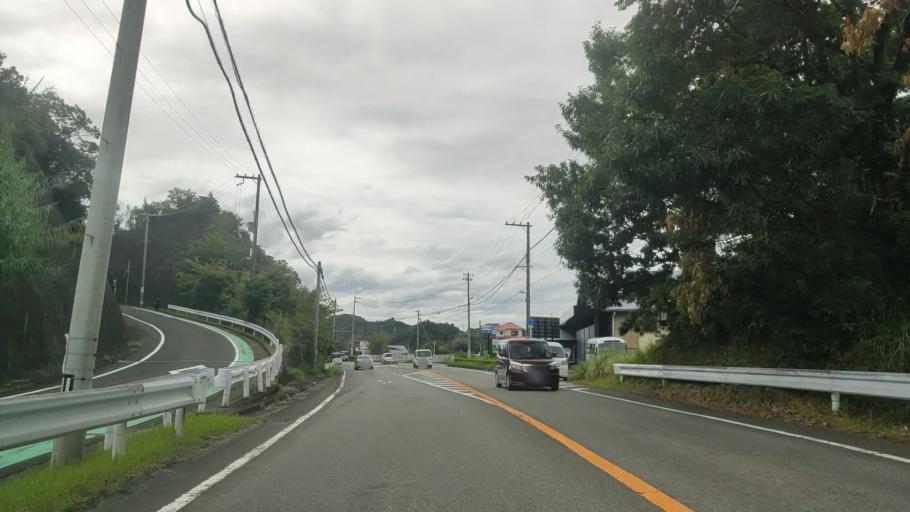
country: JP
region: Wakayama
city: Tanabe
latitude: 33.6976
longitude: 135.3883
